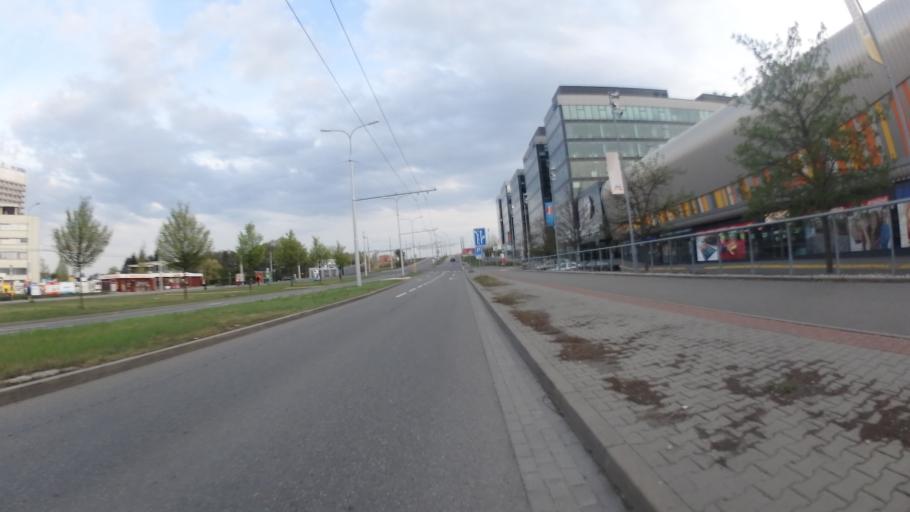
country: CZ
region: South Moravian
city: Ostopovice
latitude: 49.1763
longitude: 16.5671
